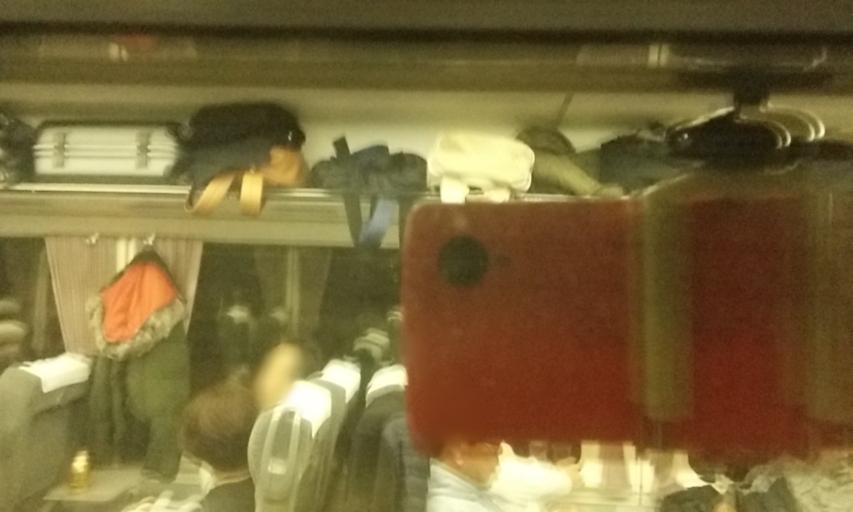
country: JP
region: Nagano
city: Ina
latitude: 35.8054
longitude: 137.6885
